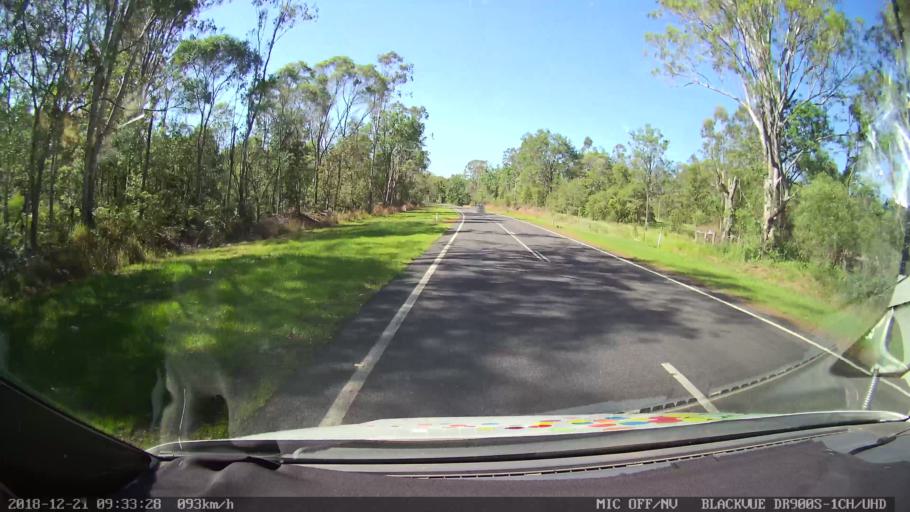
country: AU
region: New South Wales
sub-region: Clarence Valley
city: Grafton
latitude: -29.4849
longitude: 152.9766
